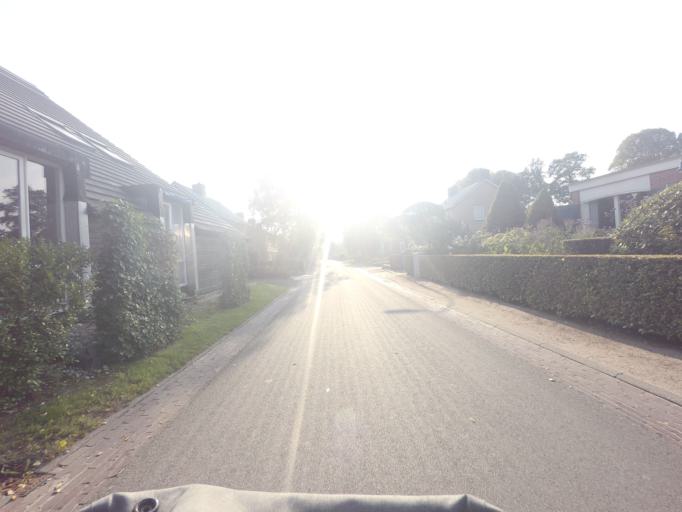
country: NL
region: Drenthe
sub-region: Gemeente Tynaarlo
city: Vries
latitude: 53.1322
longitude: 6.5648
